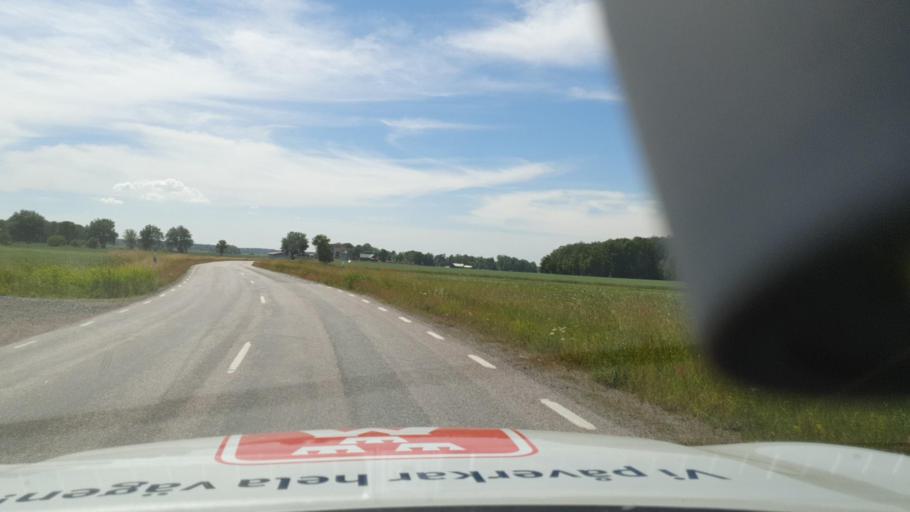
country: SE
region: Vaestra Goetaland
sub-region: Lidkopings Kommun
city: Lidkoping
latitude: 58.5141
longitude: 13.0563
